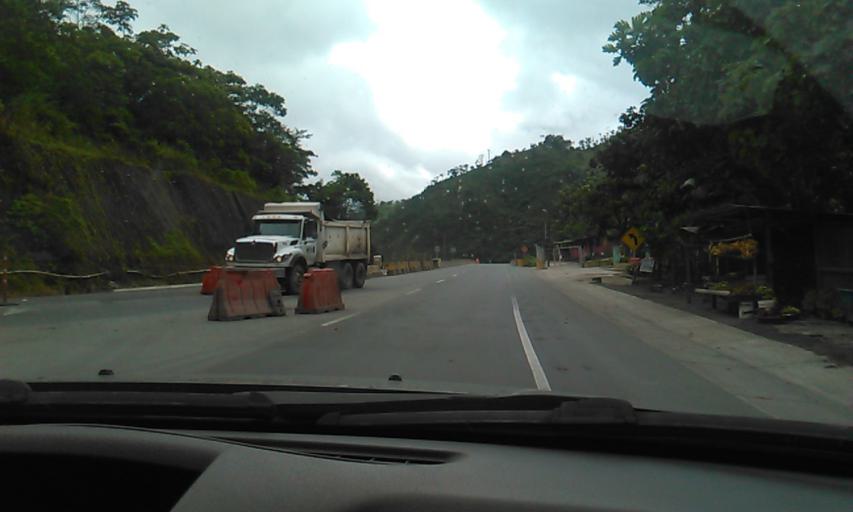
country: CO
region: Valle del Cauca
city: Dagua
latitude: 3.8080
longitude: -76.7773
